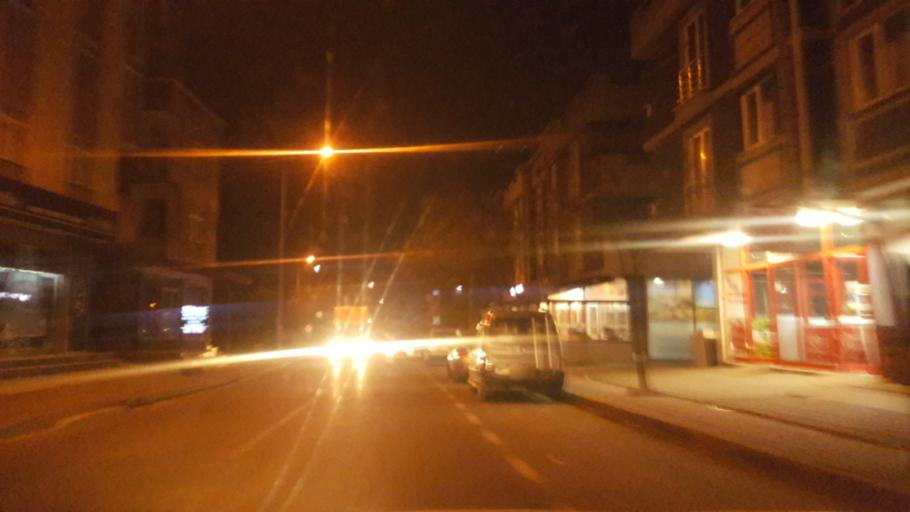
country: TR
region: Kocaeli
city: Darica
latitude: 40.7791
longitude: 29.3895
